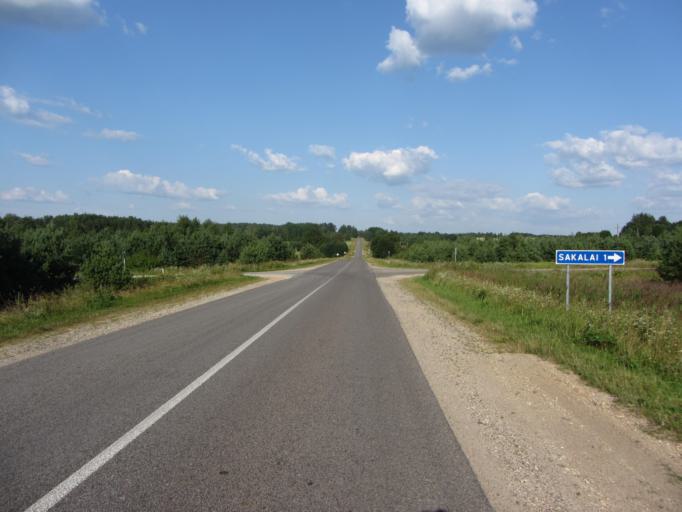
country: LT
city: Salcininkai
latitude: 54.4458
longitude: 25.3808
